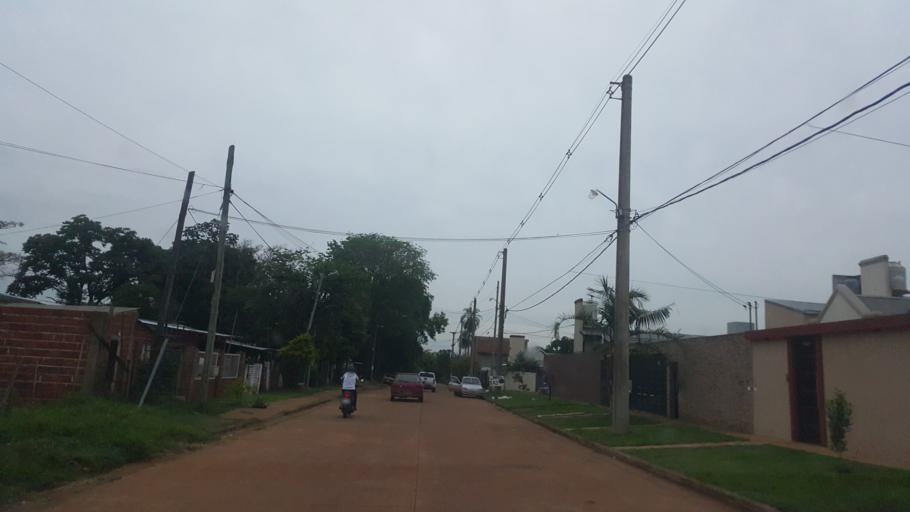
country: AR
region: Misiones
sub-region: Departamento de Capital
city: Posadas
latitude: -27.3603
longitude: -55.9364
